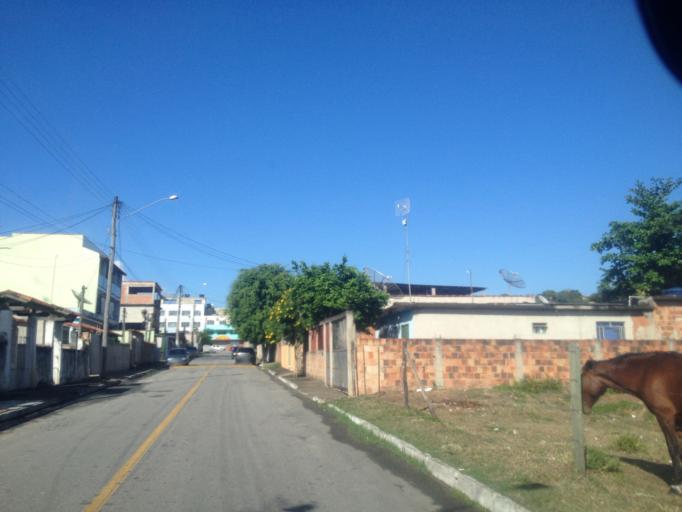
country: BR
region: Rio de Janeiro
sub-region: Porto Real
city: Porto Real
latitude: -22.4410
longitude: -44.3143
